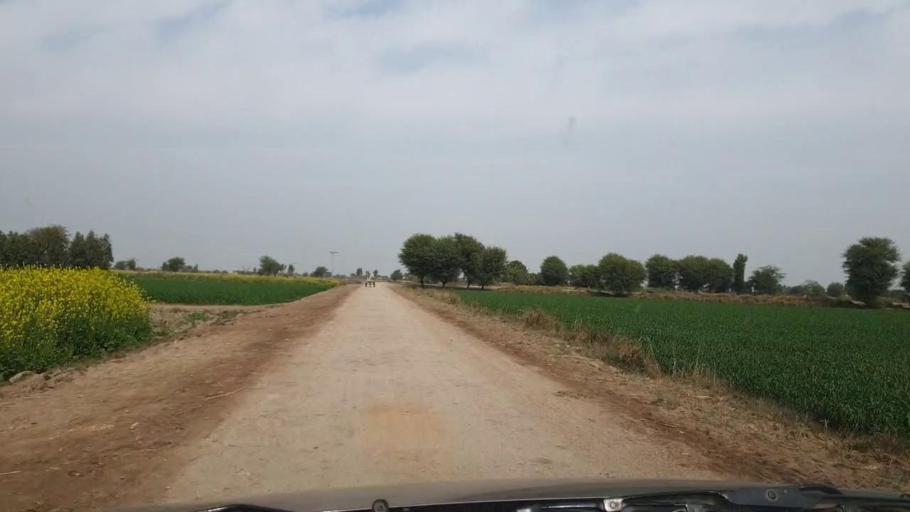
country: PK
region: Sindh
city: Sanghar
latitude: 26.0978
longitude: 68.8814
